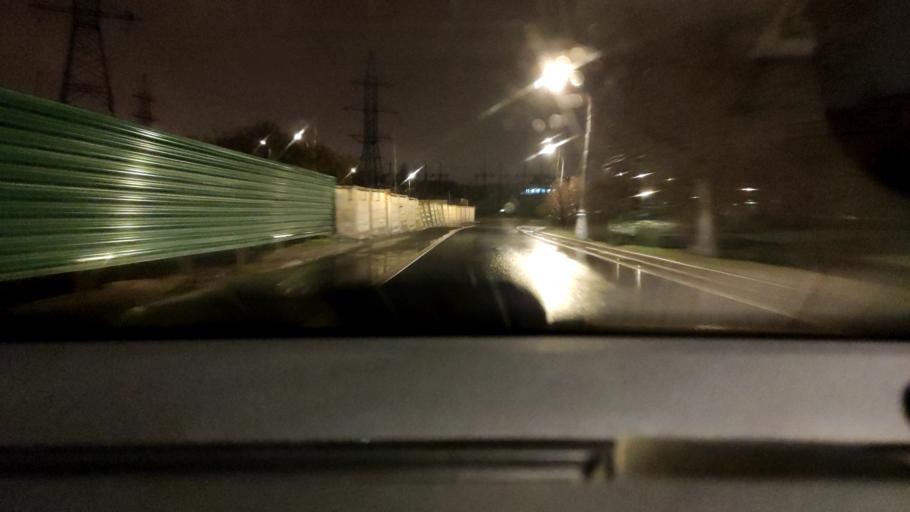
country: RU
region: Moskovskaya
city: Kuskovo
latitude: 55.7460
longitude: 37.8402
